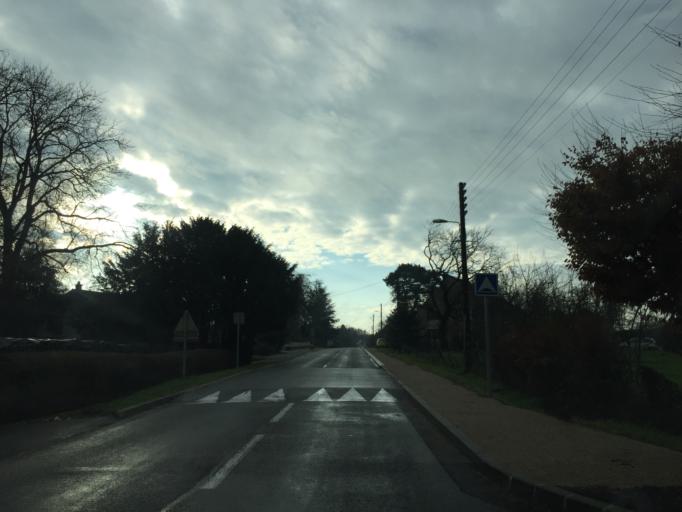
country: FR
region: Franche-Comte
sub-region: Departement du Jura
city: Mont-sous-Vaudrey
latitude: 46.9736
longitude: 5.6043
